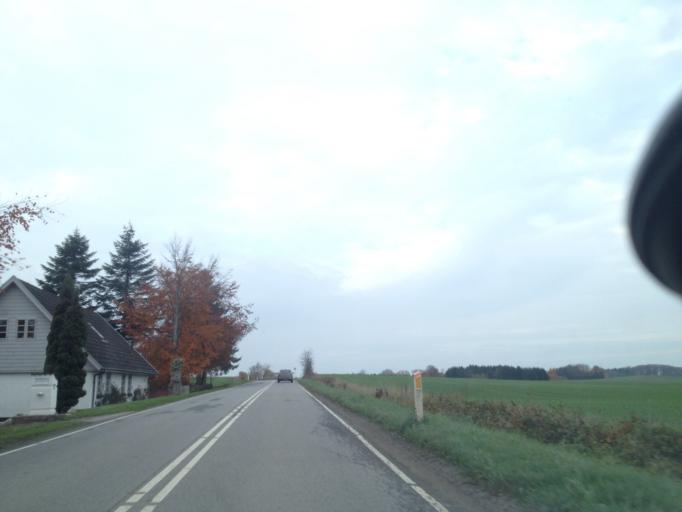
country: DK
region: South Denmark
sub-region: Assens Kommune
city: Vissenbjerg
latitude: 55.4555
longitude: 10.1185
